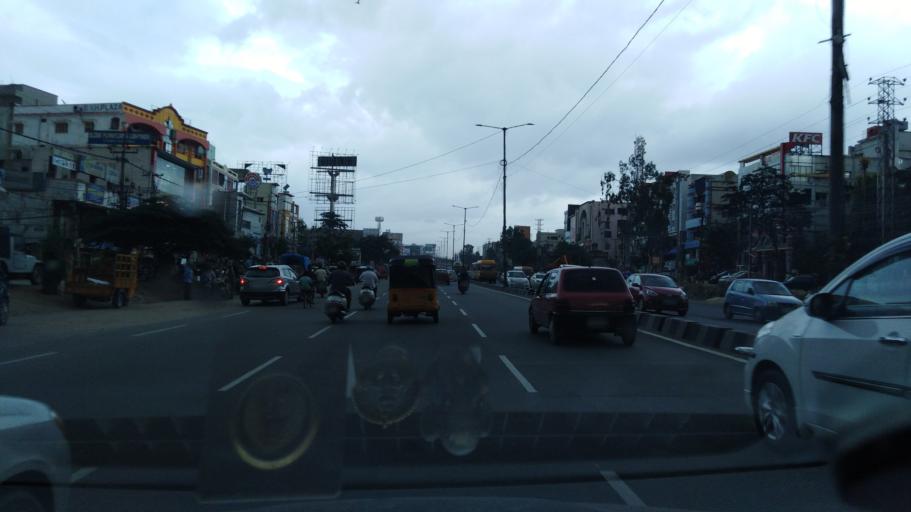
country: IN
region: Telangana
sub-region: Medak
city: Serilingampalle
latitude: 17.4951
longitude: 78.3550
